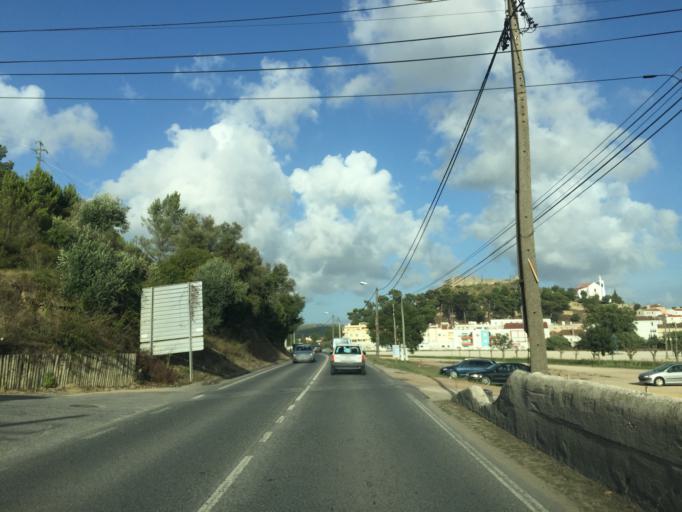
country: PT
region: Lisbon
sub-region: Torres Vedras
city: Torres Vedras
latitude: 39.0959
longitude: -9.2663
